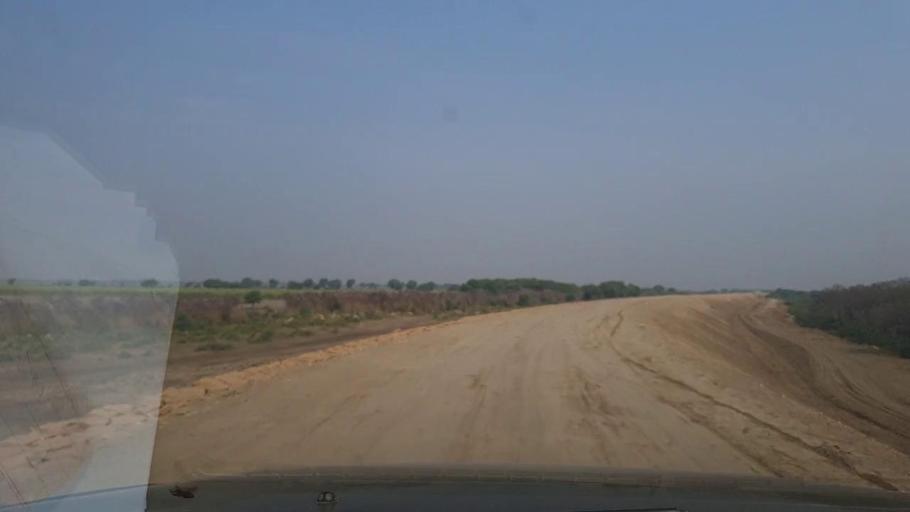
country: PK
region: Sindh
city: Bulri
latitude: 24.9740
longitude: 68.2908
